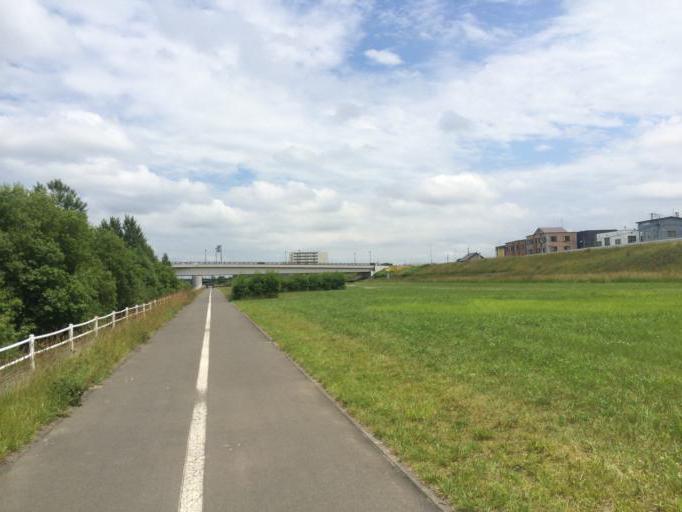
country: JP
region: Hokkaido
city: Sapporo
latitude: 43.0659
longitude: 141.3835
